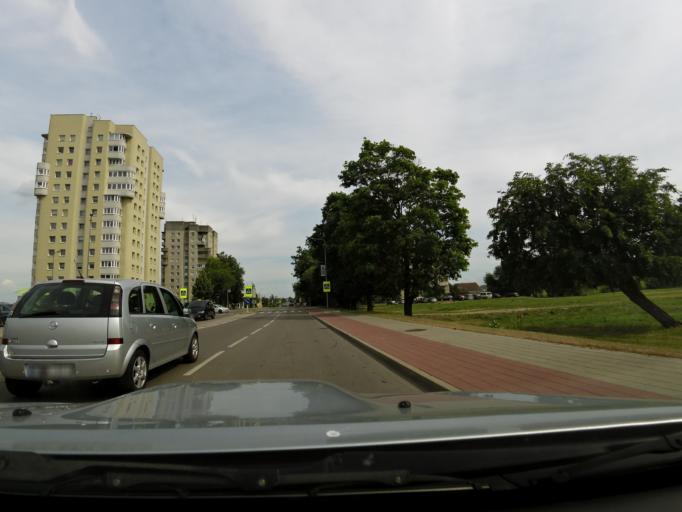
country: LT
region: Marijampoles apskritis
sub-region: Marijampole Municipality
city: Marijampole
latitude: 54.5629
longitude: 23.3324
